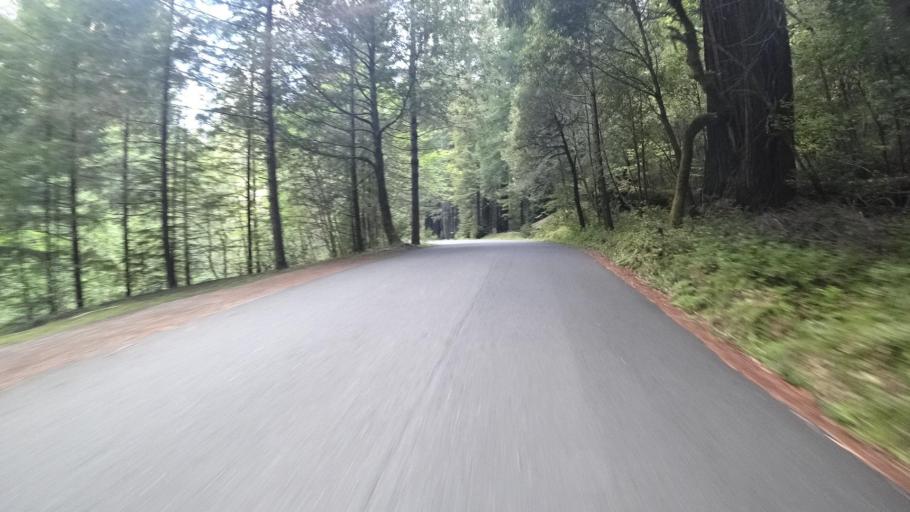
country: US
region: California
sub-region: Humboldt County
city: Rio Dell
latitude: 40.3513
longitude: -123.9777
